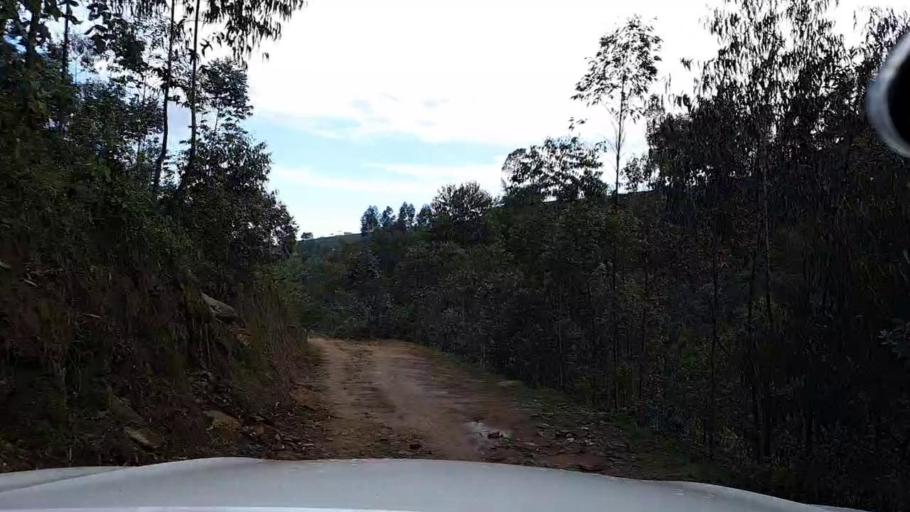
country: BI
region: Kayanza
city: Kayanza
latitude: -2.7791
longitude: 29.4483
